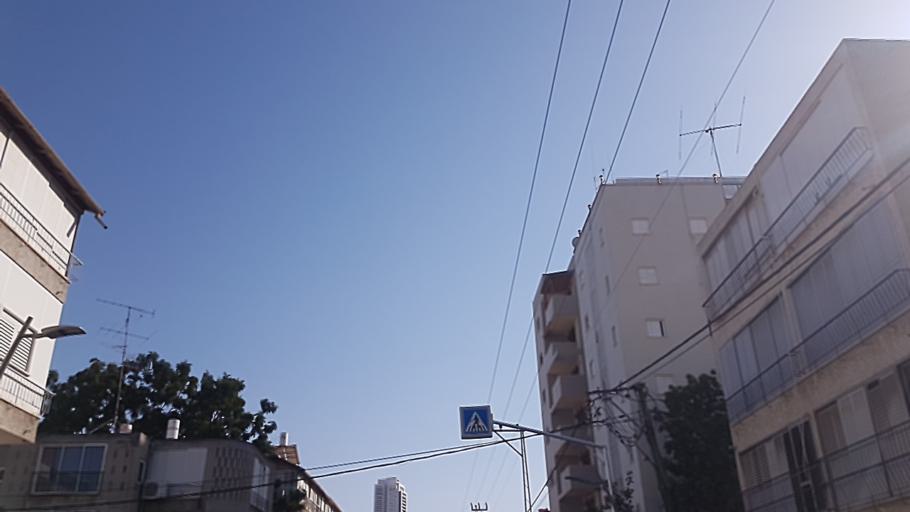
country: IL
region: Tel Aviv
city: Bene Beraq
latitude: 32.0768
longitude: 34.8231
